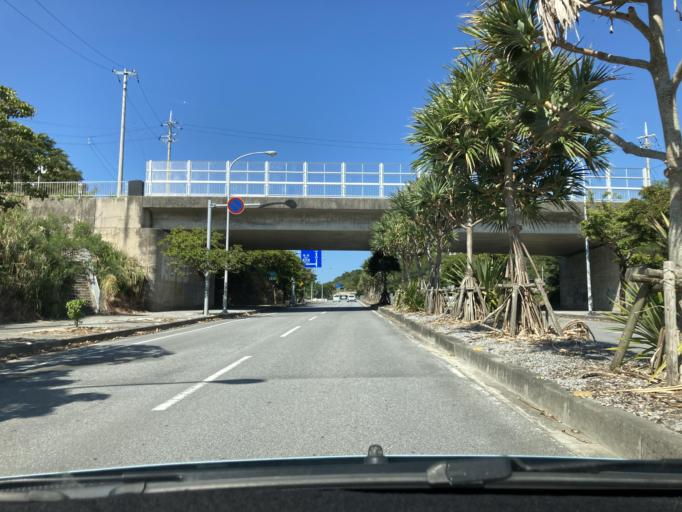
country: JP
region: Okinawa
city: Tomigusuku
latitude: 26.1834
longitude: 127.7226
